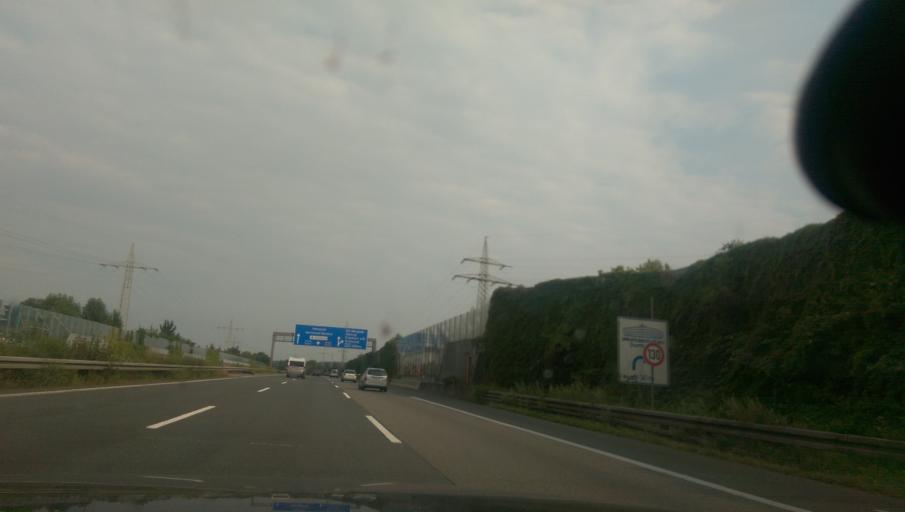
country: DE
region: North Rhine-Westphalia
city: Castrop-Rauxel
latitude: 51.5952
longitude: 7.3410
